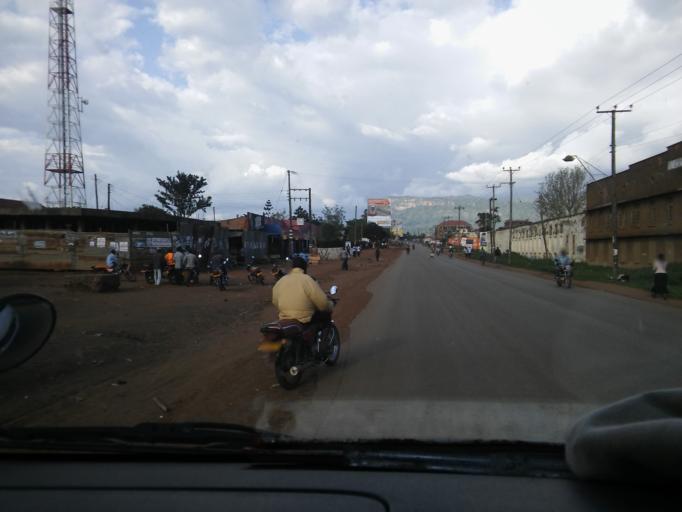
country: UG
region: Eastern Region
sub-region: Mbale District
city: Mbale
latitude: 1.0795
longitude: 34.1635
